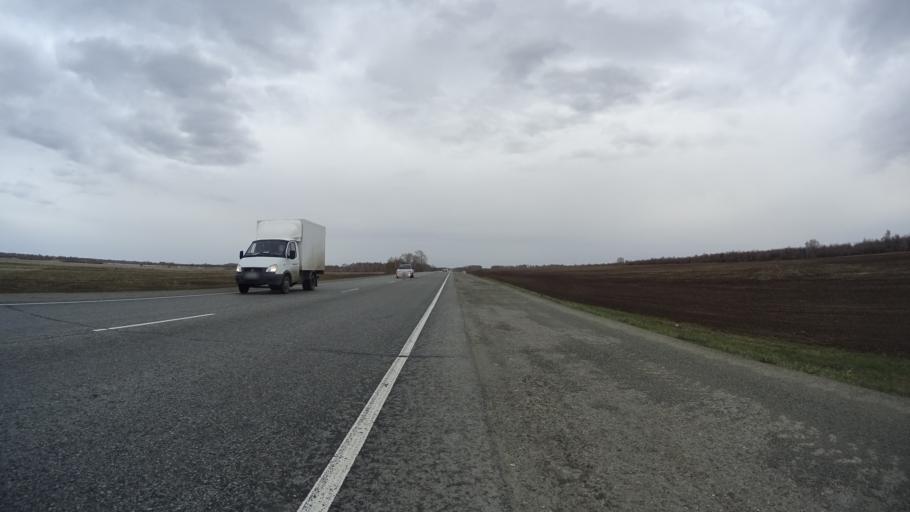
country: RU
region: Chelyabinsk
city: Krasnogorskiy
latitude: 54.6672
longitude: 61.2521
